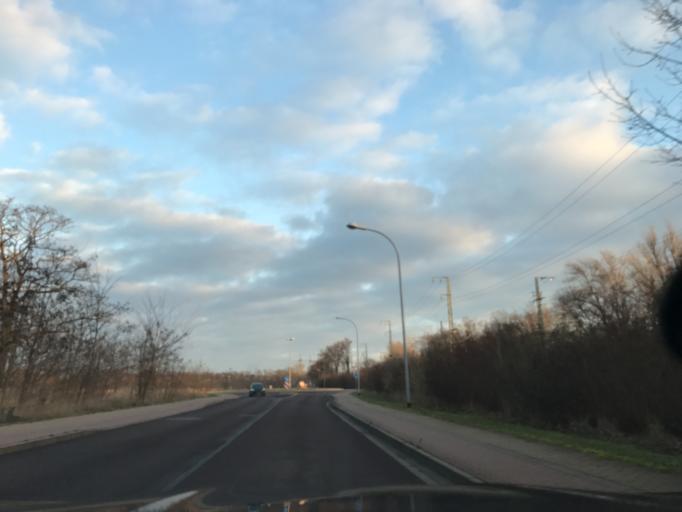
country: DE
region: Brandenburg
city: Wusterwitz
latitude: 52.3828
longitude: 12.3995
